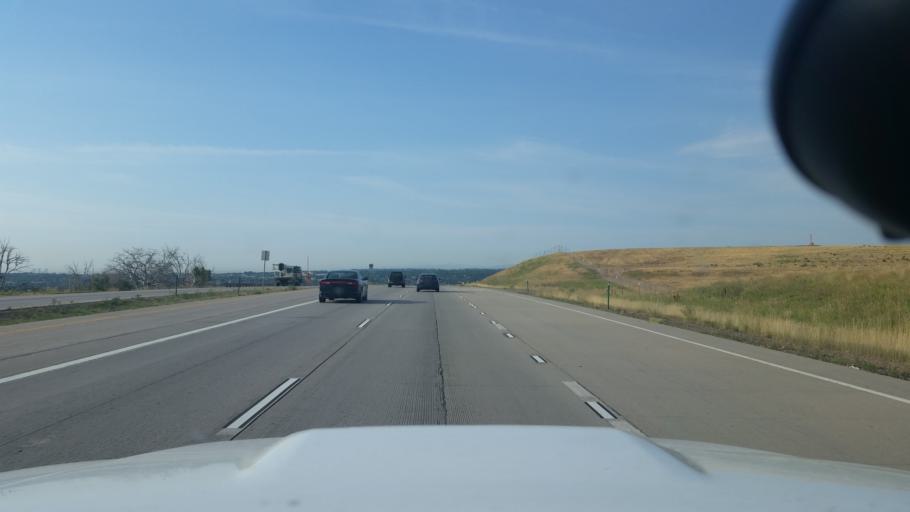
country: US
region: Colorado
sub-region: Broomfield County
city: Broomfield
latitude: 39.9006
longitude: -105.0962
